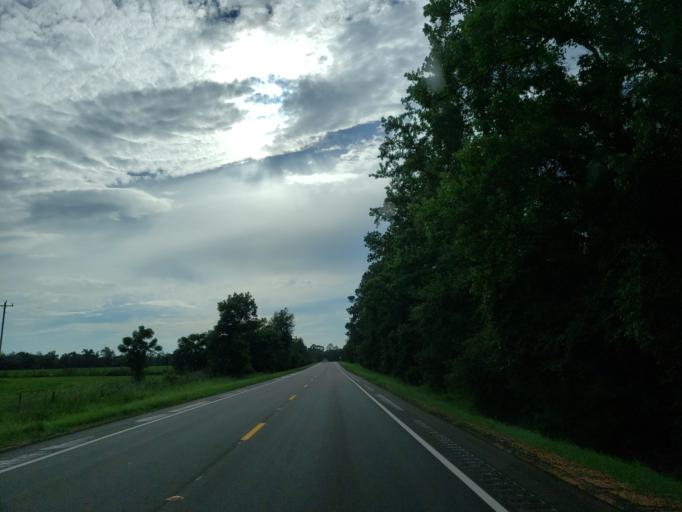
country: US
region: Georgia
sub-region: Irwin County
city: Ocilla
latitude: 31.5640
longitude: -83.3336
